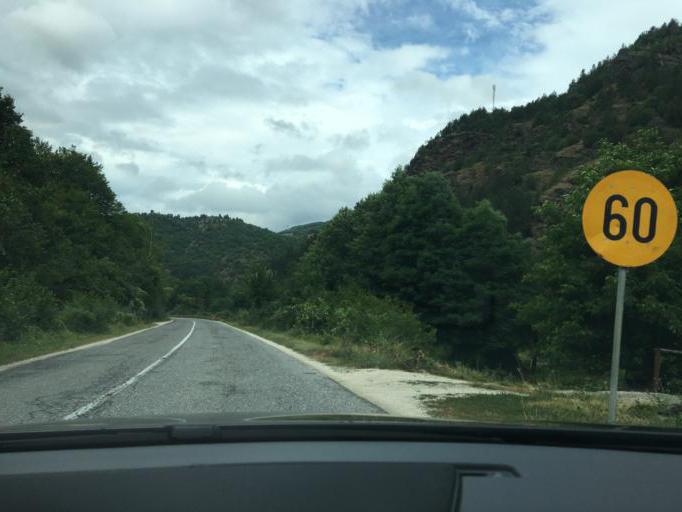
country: MK
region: Kriva Palanka
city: Kriva Palanka
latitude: 42.2304
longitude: 22.3714
